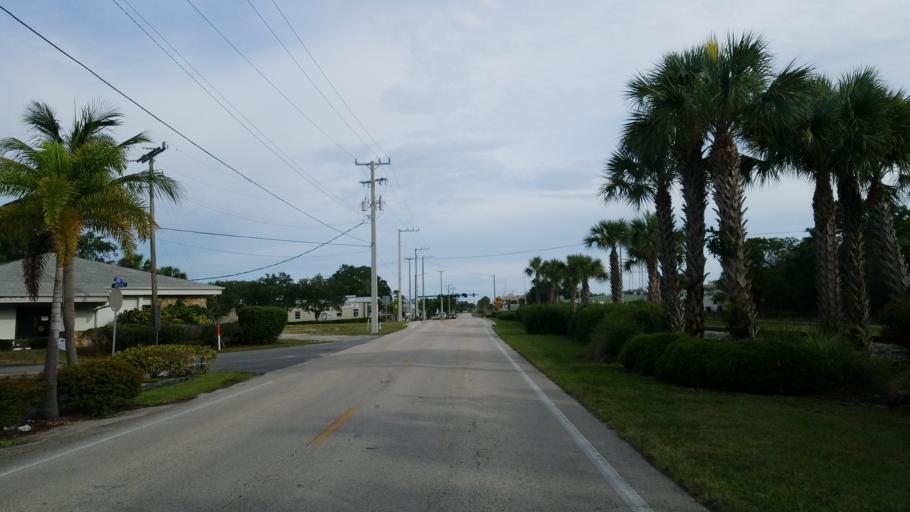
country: US
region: Florida
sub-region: Martin County
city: Stuart
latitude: 27.1926
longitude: -80.2481
